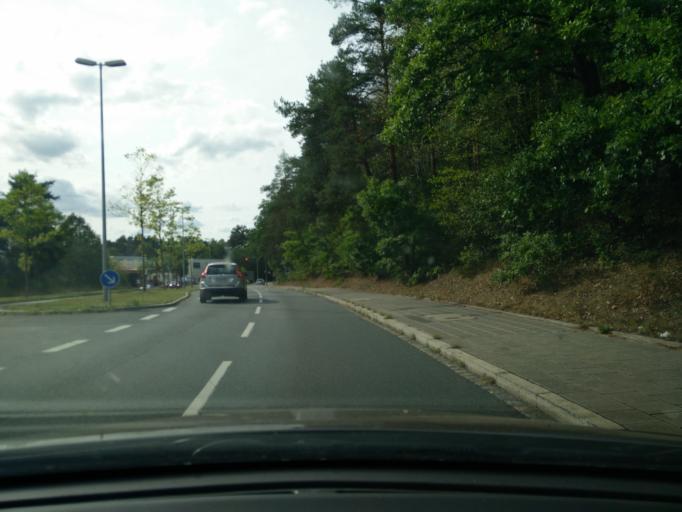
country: DE
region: Bavaria
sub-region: Regierungsbezirk Mittelfranken
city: Wendelstein
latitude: 49.4150
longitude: 11.1411
